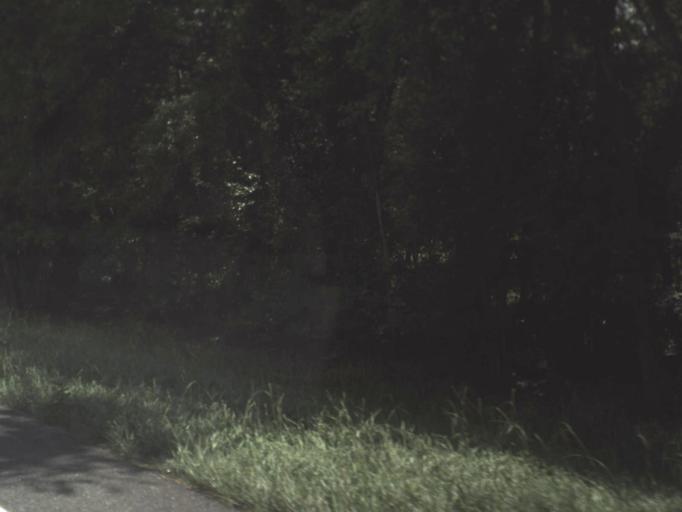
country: US
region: Florida
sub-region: Columbia County
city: Watertown
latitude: 30.0889
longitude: -82.6019
